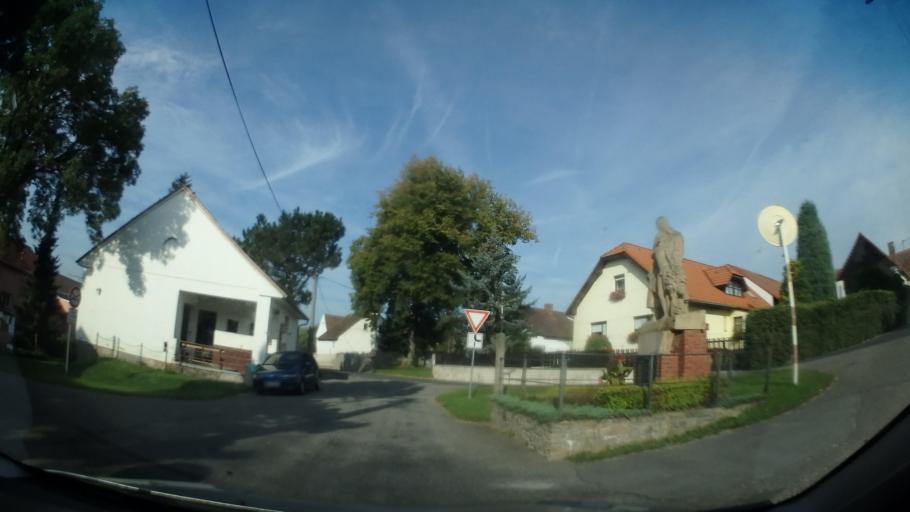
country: CZ
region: Jihocesky
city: Cimelice
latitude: 49.4215
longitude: 14.1168
